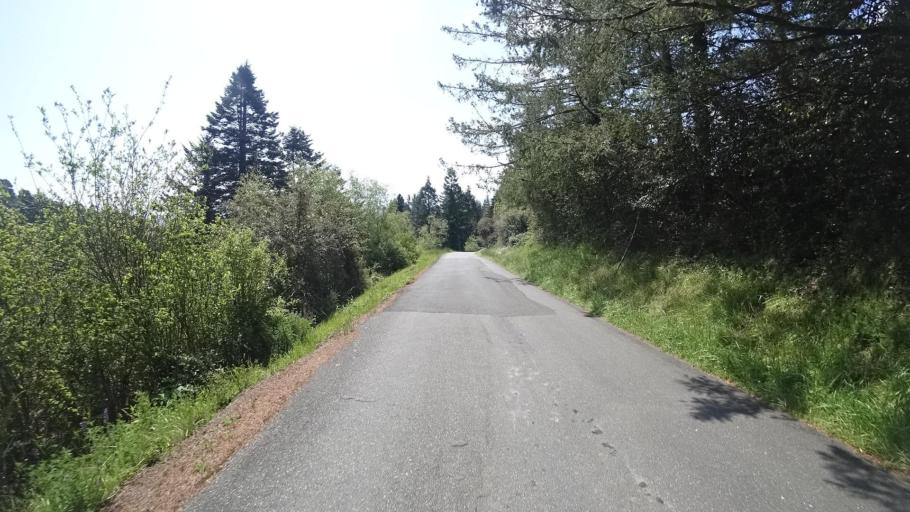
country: US
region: California
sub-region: Humboldt County
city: Fortuna
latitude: 40.6086
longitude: -124.1822
